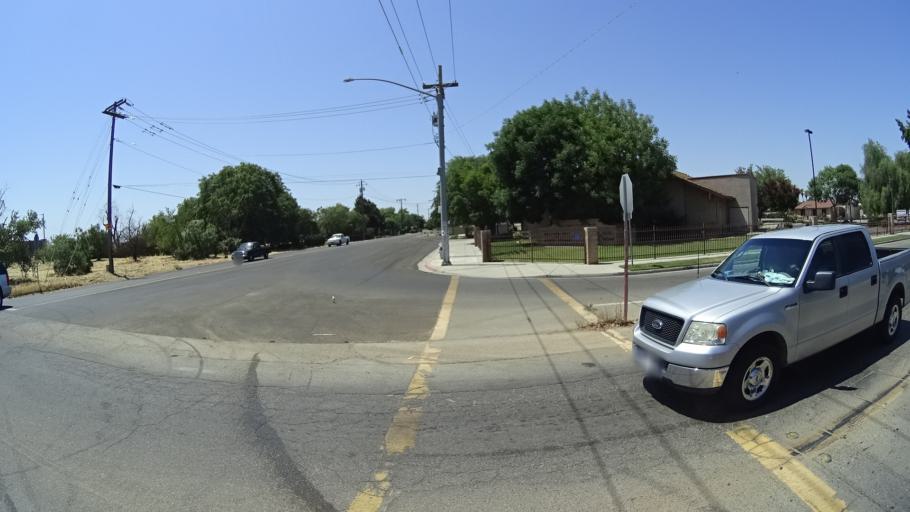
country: US
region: California
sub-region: Fresno County
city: Sunnyside
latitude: 36.7146
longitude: -119.7277
